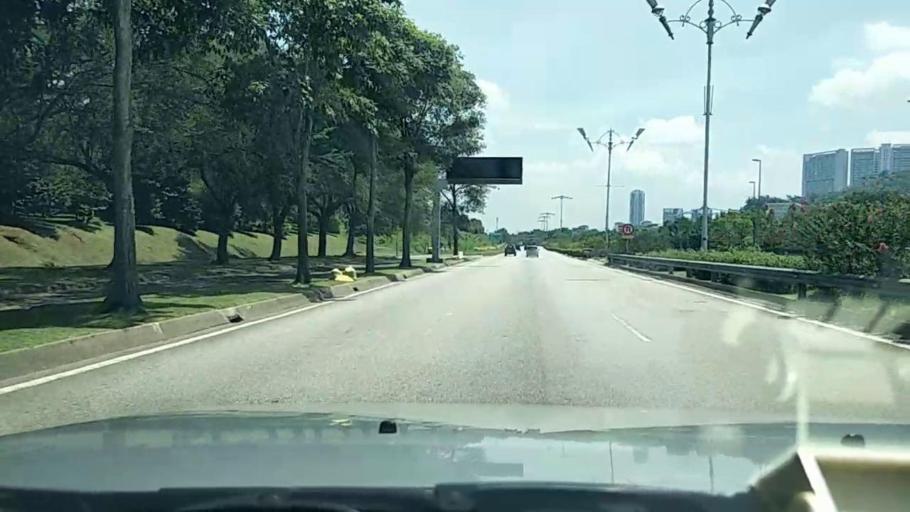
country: MY
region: Putrajaya
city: Putrajaya
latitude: 2.9461
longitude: 101.6752
